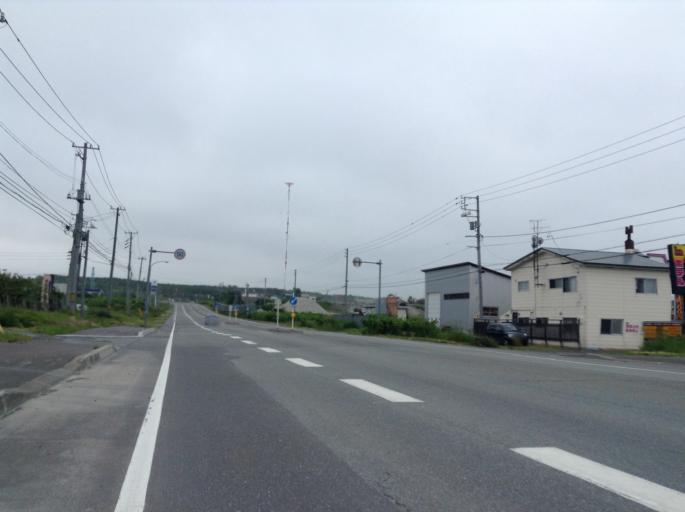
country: JP
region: Hokkaido
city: Wakkanai
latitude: 45.3798
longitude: 141.7101
